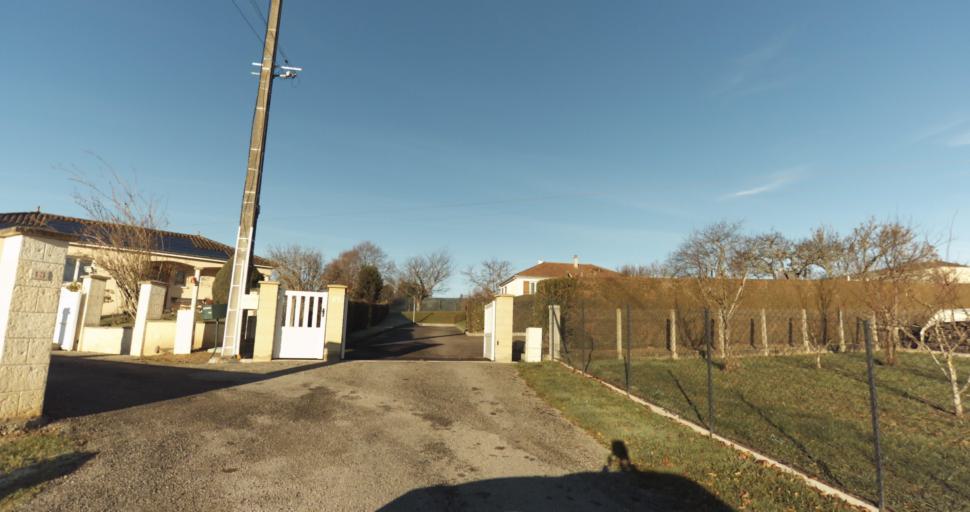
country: FR
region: Limousin
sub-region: Departement de la Haute-Vienne
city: Aixe-sur-Vienne
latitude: 45.8090
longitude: 1.1381
